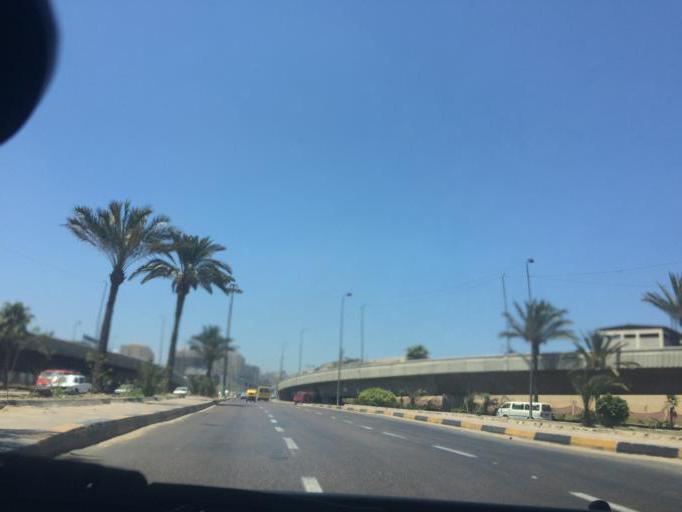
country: EG
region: Alexandria
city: Alexandria
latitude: 31.1810
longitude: 29.9282
